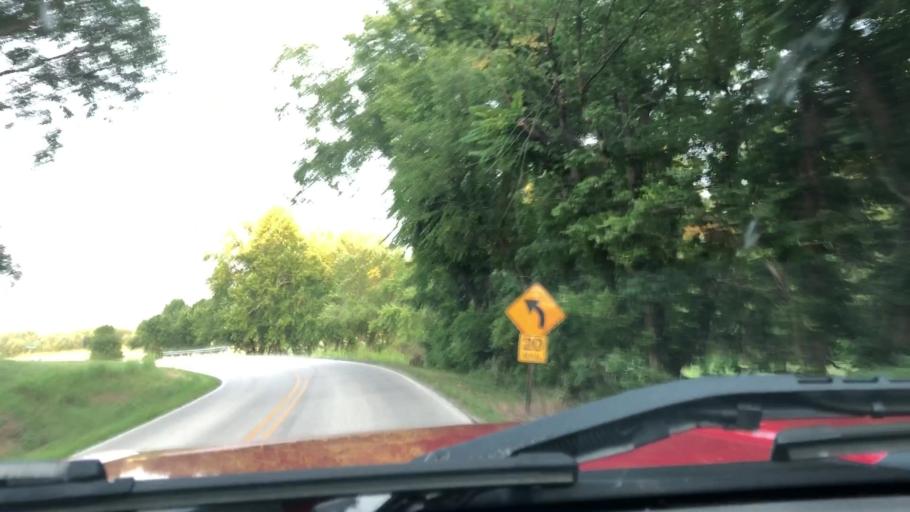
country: US
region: Missouri
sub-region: Jasper County
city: Duquesne
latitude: 37.0151
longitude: -94.4943
